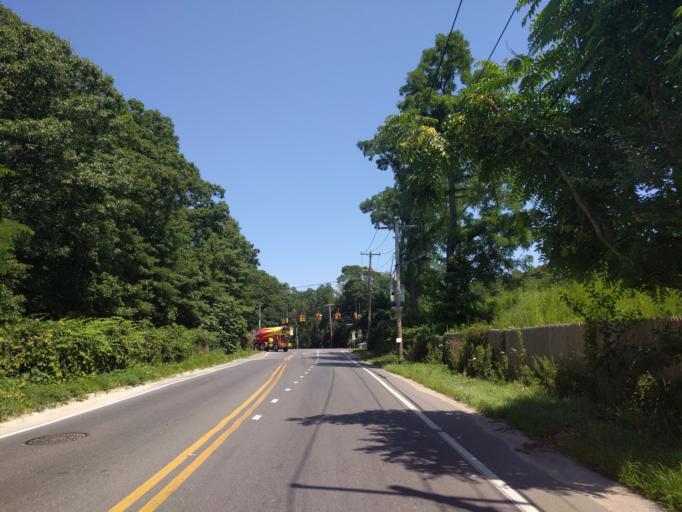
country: US
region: New York
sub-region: Suffolk County
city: Kings Park
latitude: 40.8830
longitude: -73.2878
